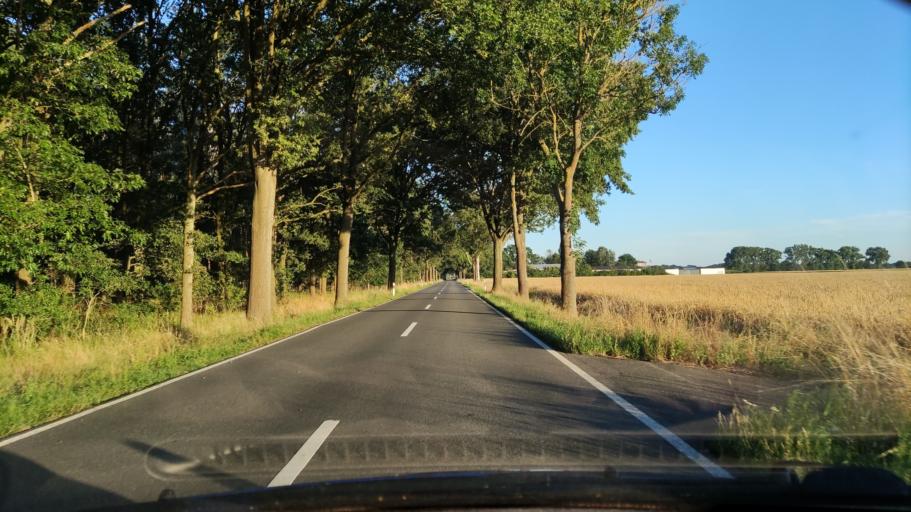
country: DE
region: Lower Saxony
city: Luechow
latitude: 53.0198
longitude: 11.1463
